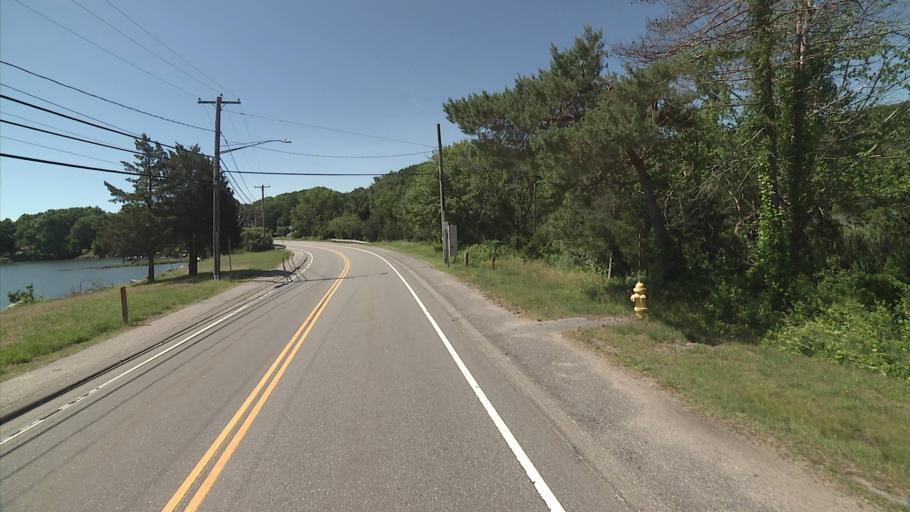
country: US
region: Connecticut
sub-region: New London County
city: Noank
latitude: 41.3333
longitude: -71.9927
